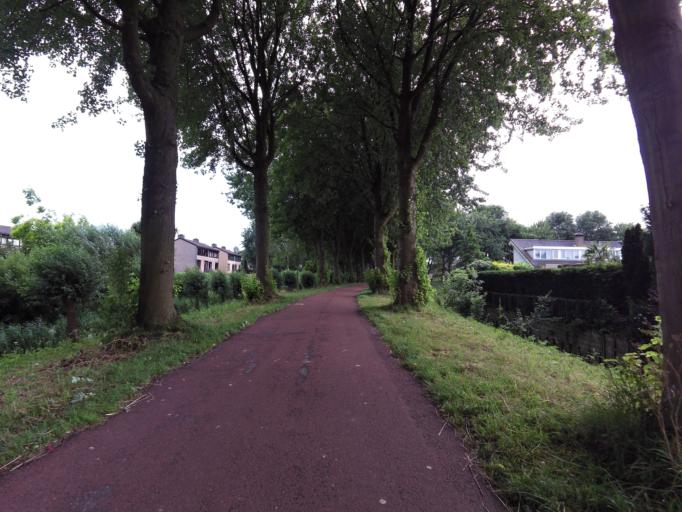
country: NL
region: South Holland
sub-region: Gemeente Dordrecht
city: Dordrecht
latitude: 51.7882
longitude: 4.7060
